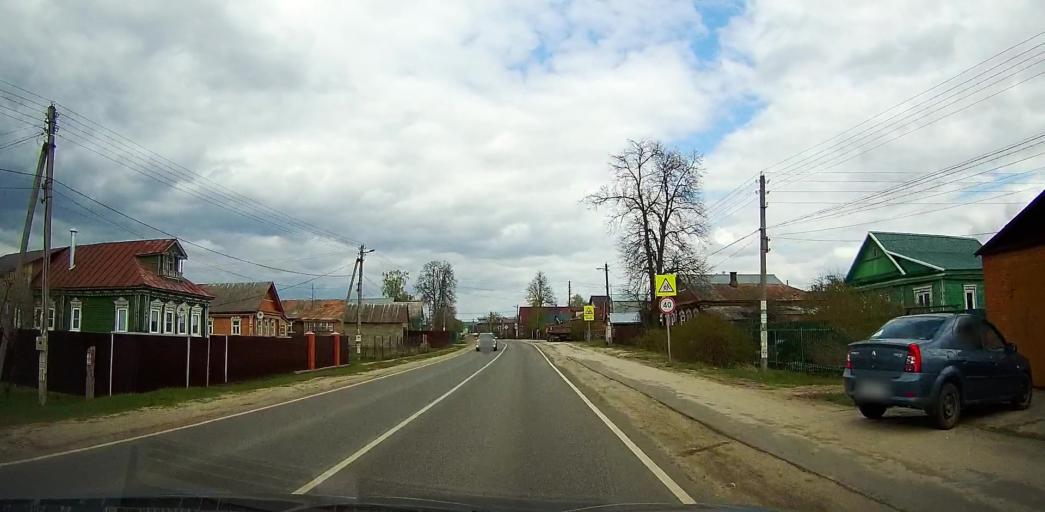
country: RU
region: Moskovskaya
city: Ashitkovo
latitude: 55.4450
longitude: 38.5908
